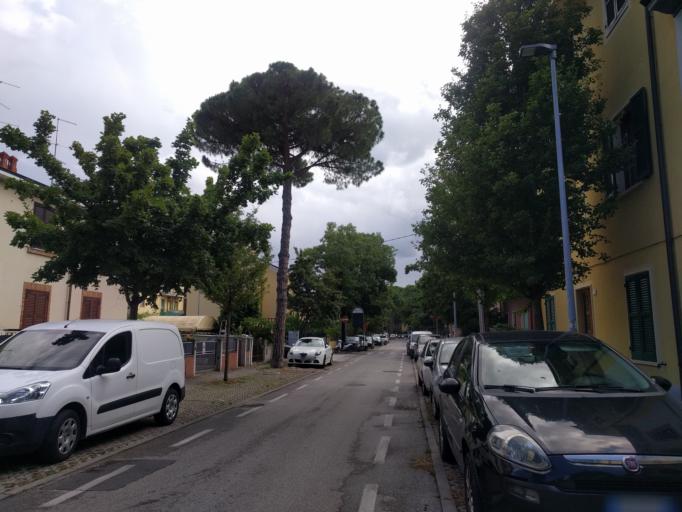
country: IT
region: The Marches
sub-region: Provincia di Pesaro e Urbino
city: Pesaro
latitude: 43.9040
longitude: 12.9098
